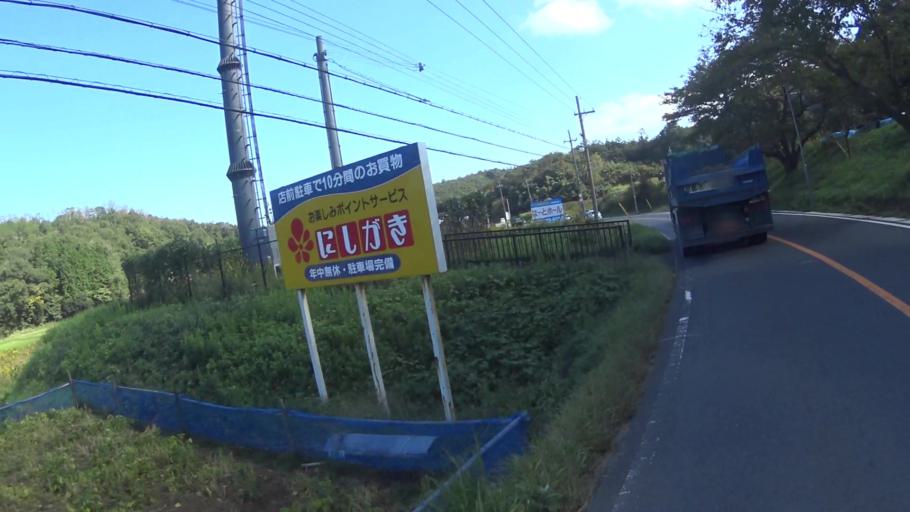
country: JP
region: Kyoto
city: Miyazu
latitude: 35.6979
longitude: 135.0582
